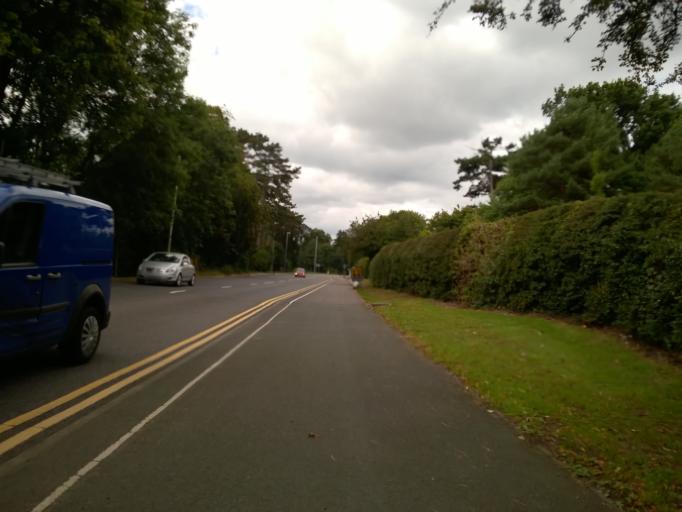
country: GB
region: England
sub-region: Leicestershire
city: Glenfield
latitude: 52.6564
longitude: -1.1920
